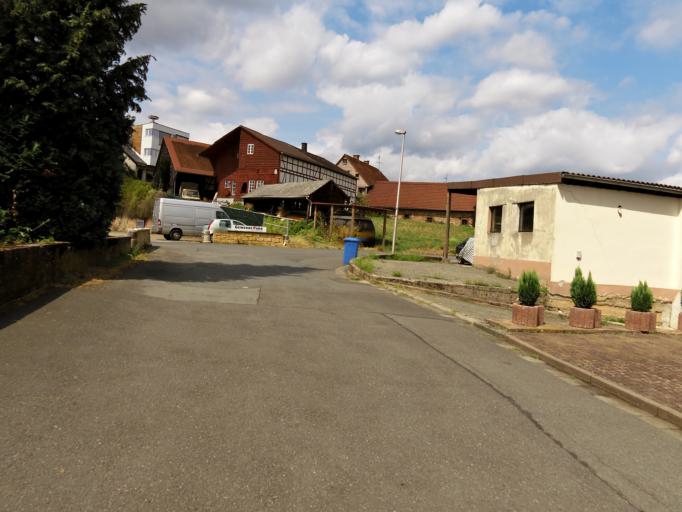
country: DE
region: Hesse
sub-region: Regierungsbezirk Darmstadt
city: Frankisch-Crumbach
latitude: 49.7195
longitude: 8.8655
